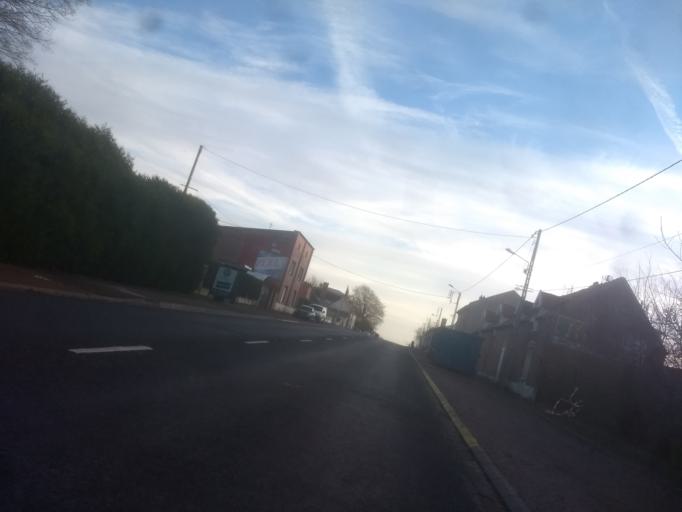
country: FR
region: Nord-Pas-de-Calais
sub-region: Departement du Pas-de-Calais
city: Beaurains
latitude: 50.2596
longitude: 2.7867
